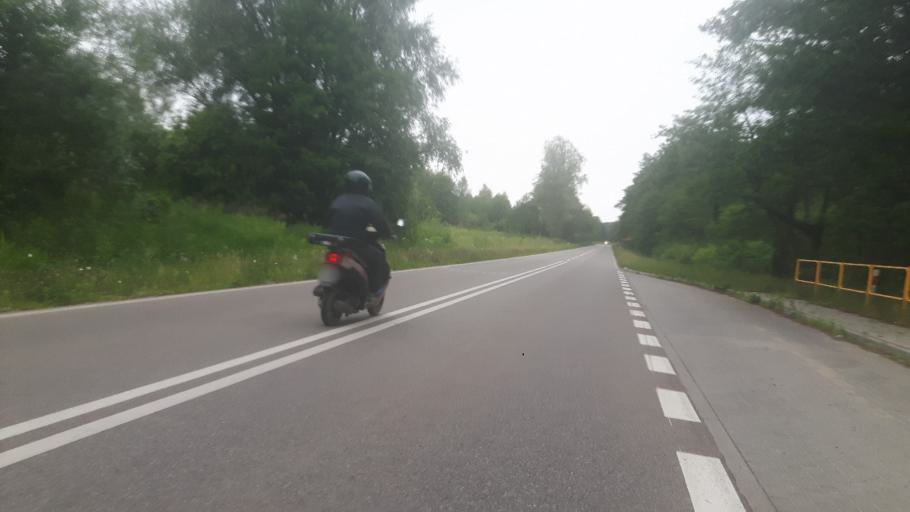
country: PL
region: Warmian-Masurian Voivodeship
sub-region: Powiat elblaski
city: Elblag
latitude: 54.2351
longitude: 19.3922
